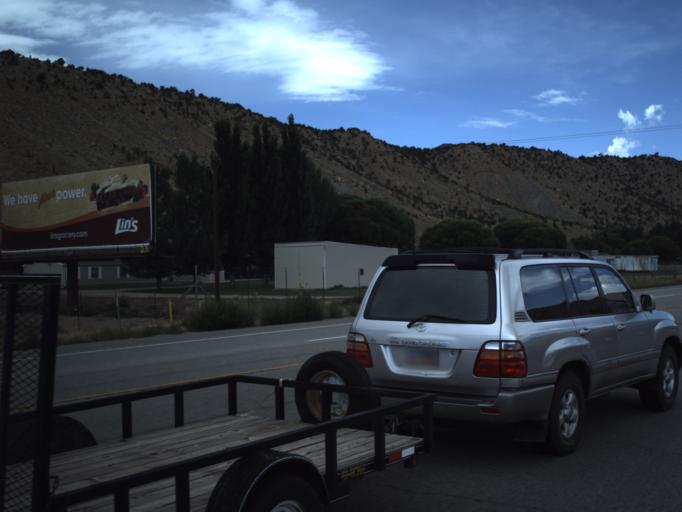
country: US
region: Utah
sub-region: Carbon County
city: Spring Glen
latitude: 39.6698
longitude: -110.8614
